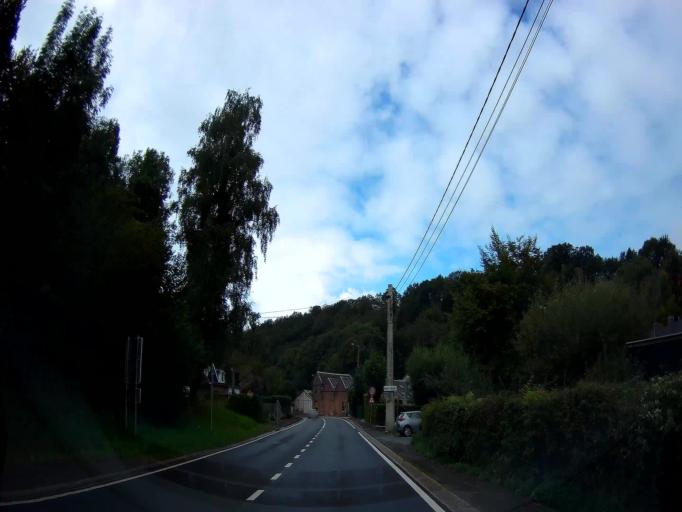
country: BE
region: Wallonia
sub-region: Province de Liege
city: Limbourg
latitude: 50.6244
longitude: 5.9542
